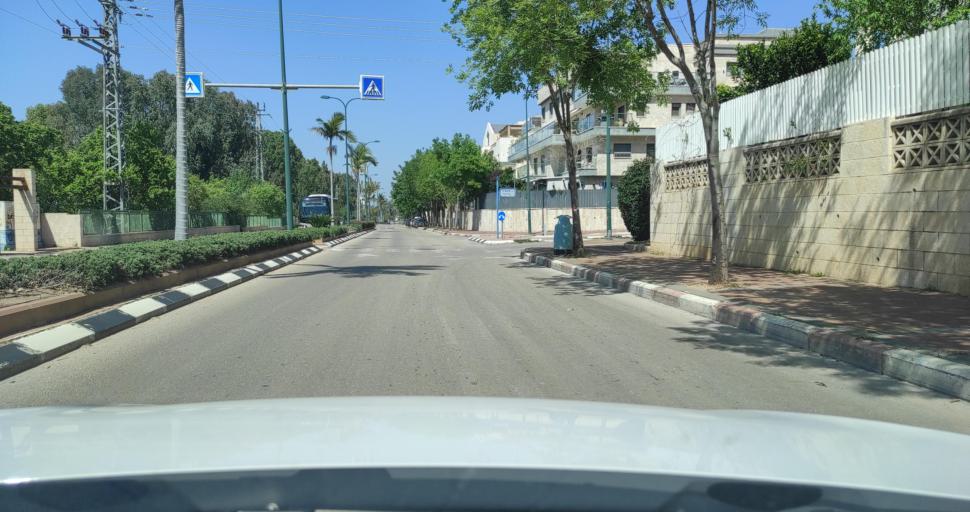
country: IL
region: Central District
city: Nordiyya
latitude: 32.3033
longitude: 34.8805
